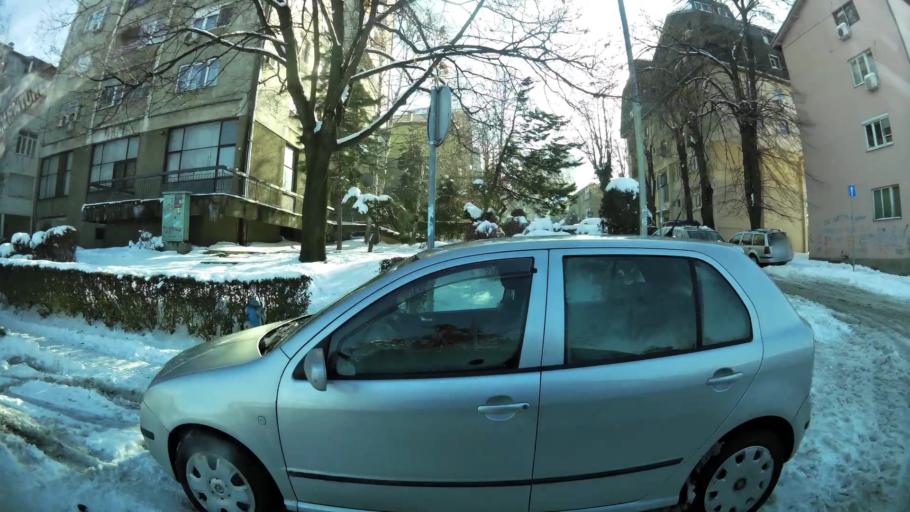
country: RS
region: Central Serbia
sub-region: Belgrade
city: Palilula
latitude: 44.8160
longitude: 20.5103
